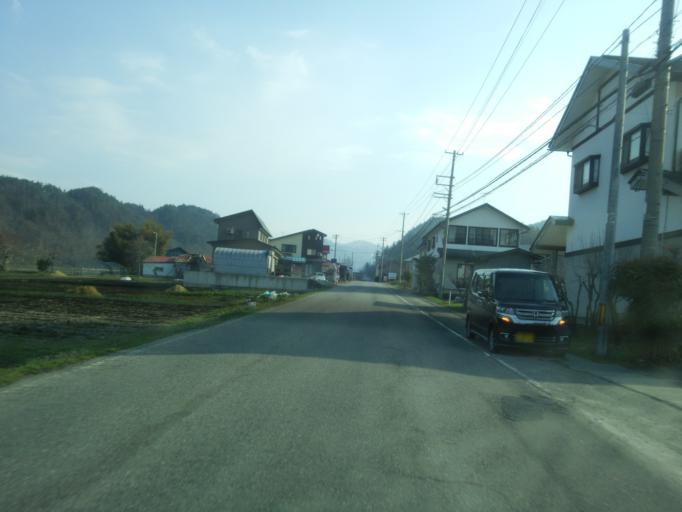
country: JP
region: Fukushima
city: Kitakata
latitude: 37.6847
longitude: 139.9029
